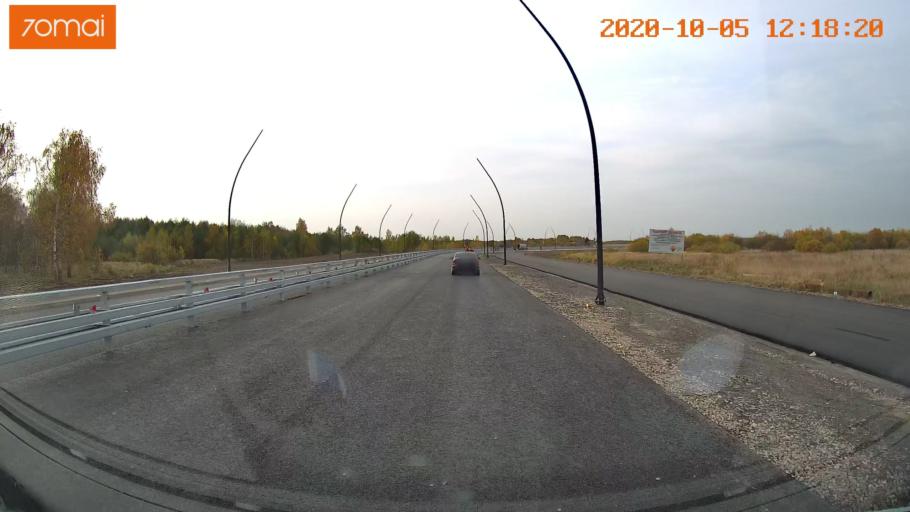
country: RU
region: Ivanovo
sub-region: Gorod Ivanovo
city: Ivanovo
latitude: 56.9522
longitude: 40.9427
